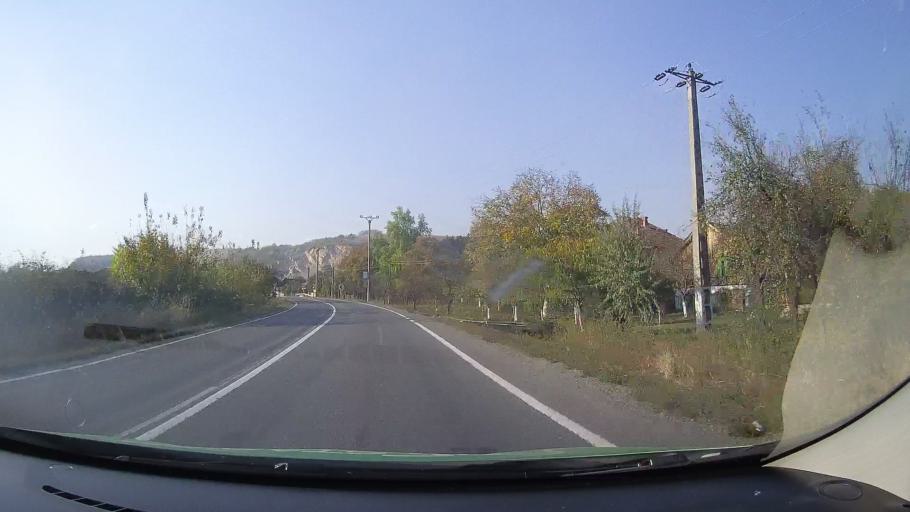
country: RO
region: Arad
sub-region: Comuna Zabrani
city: Neudorf
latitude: 46.1056
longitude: 21.6390
